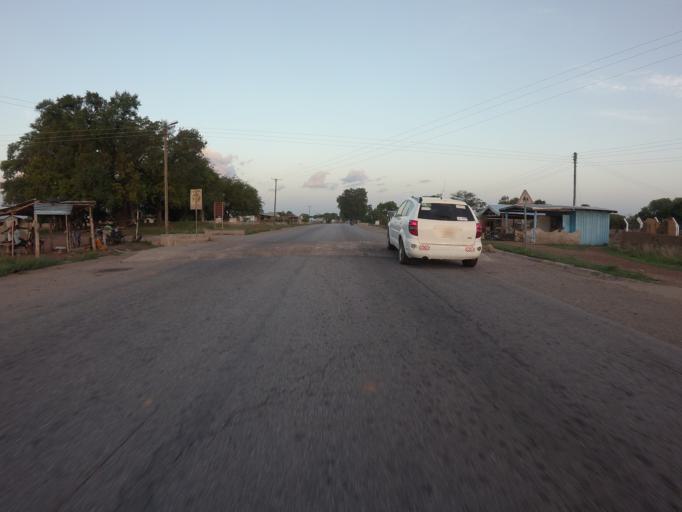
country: GH
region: Upper East
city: Navrongo
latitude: 10.8593
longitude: -1.0298
